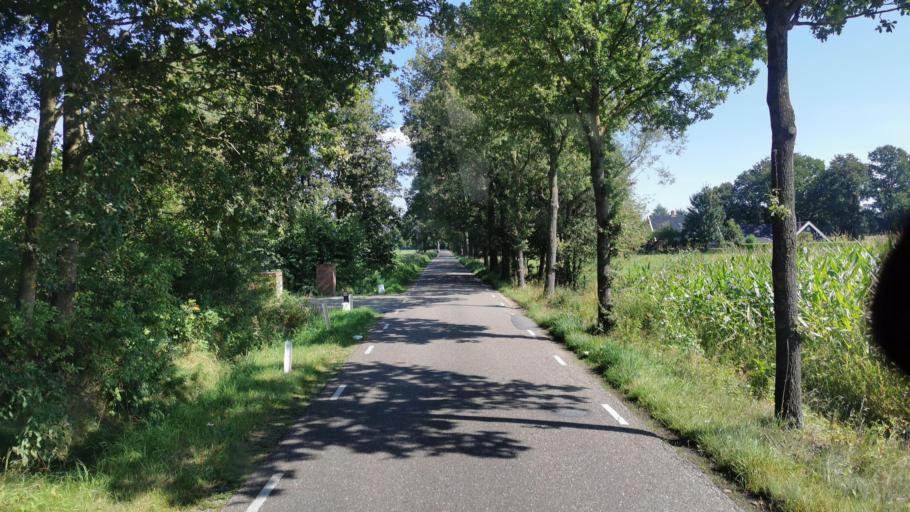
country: NL
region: Overijssel
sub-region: Gemeente Enschede
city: Enschede
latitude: 52.1992
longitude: 6.9537
